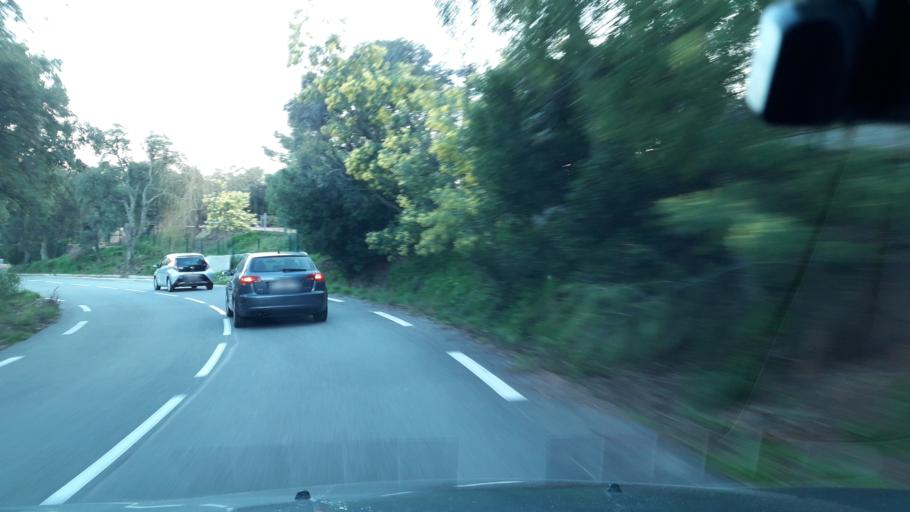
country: FR
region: Provence-Alpes-Cote d'Azur
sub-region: Departement du Var
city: Saint-Raphael
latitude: 43.4816
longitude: 6.7764
